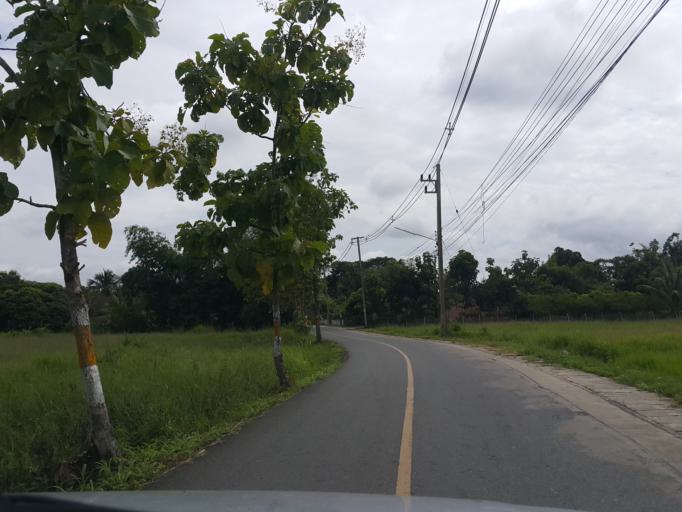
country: TH
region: Chiang Mai
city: San Kamphaeng
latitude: 18.8418
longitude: 99.1470
